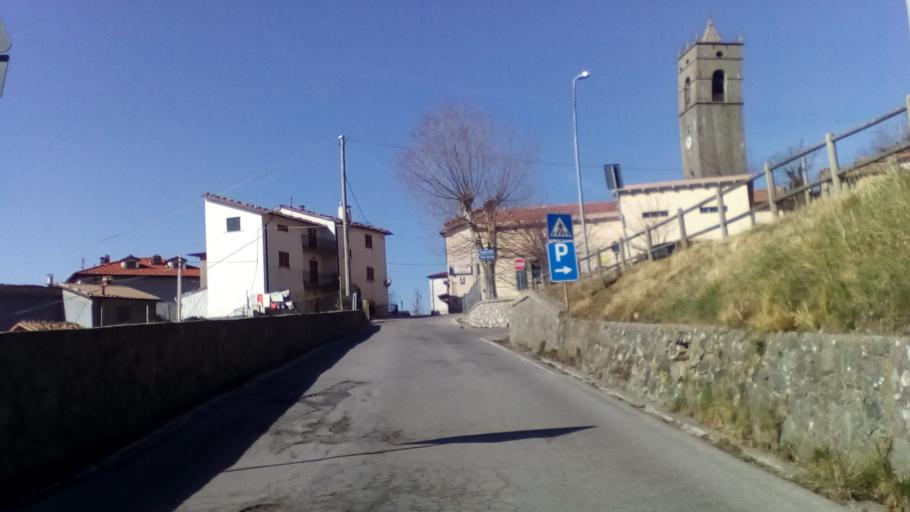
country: IT
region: Tuscany
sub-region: Provincia di Lucca
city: Castiglione di Garfagnana
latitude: 44.1556
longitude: 10.4389
